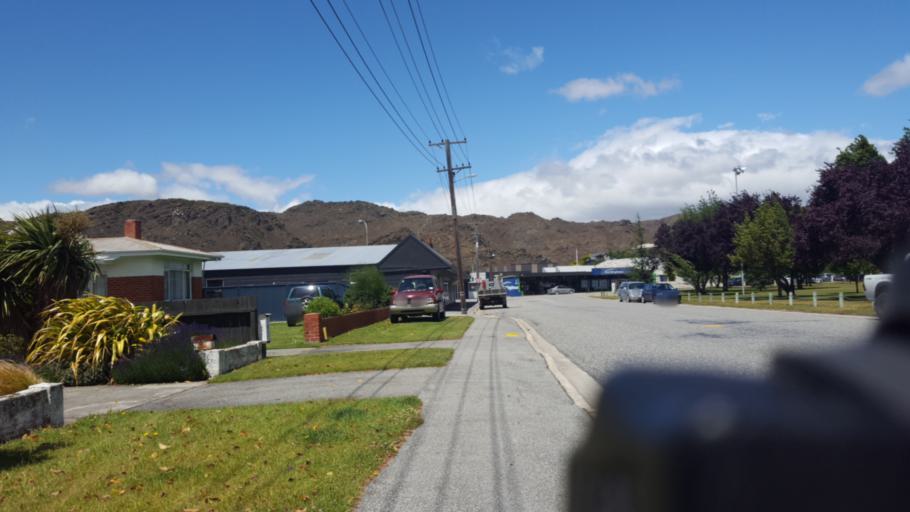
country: NZ
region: Otago
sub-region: Queenstown-Lakes District
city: Wanaka
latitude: -45.2527
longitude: 169.3936
